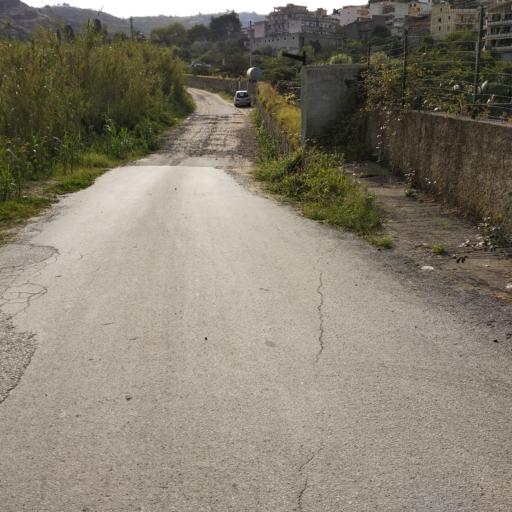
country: IT
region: Sicily
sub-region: Messina
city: Villafranca Tirrena
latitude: 38.2335
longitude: 15.4353
